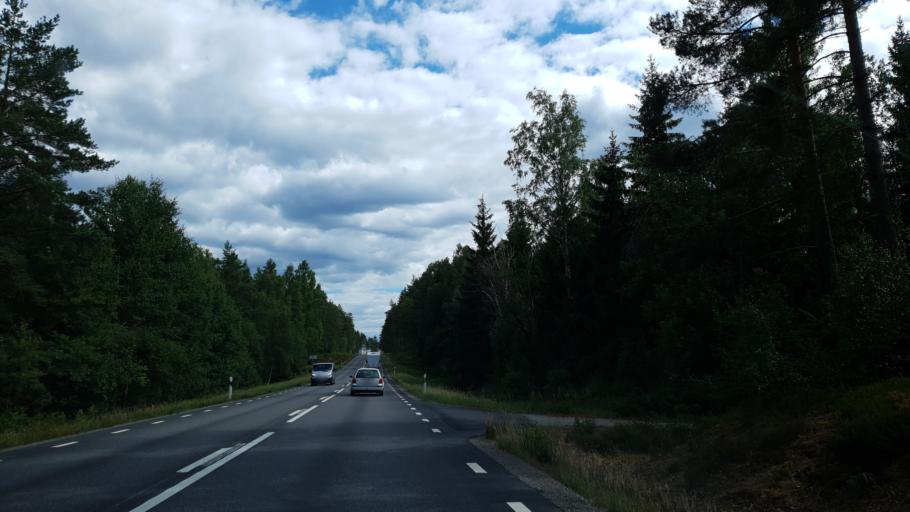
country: SE
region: Kronoberg
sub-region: Lessebo Kommun
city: Lessebo
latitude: 56.8230
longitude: 15.4058
